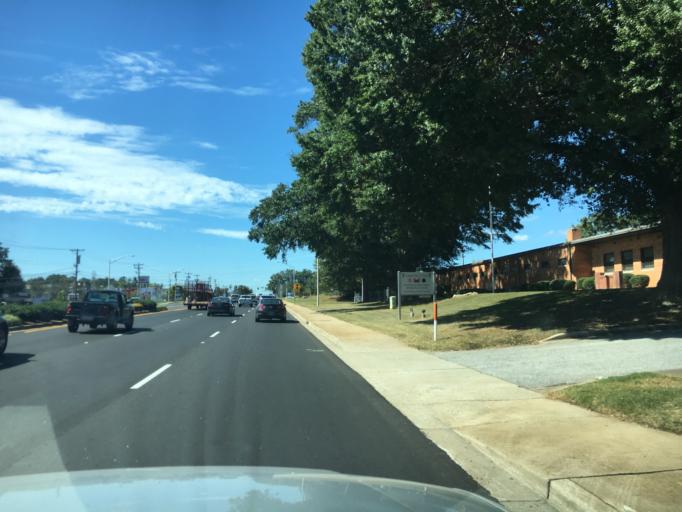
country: US
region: South Carolina
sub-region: Spartanburg County
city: Arcadia
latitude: 34.9379
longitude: -81.9769
